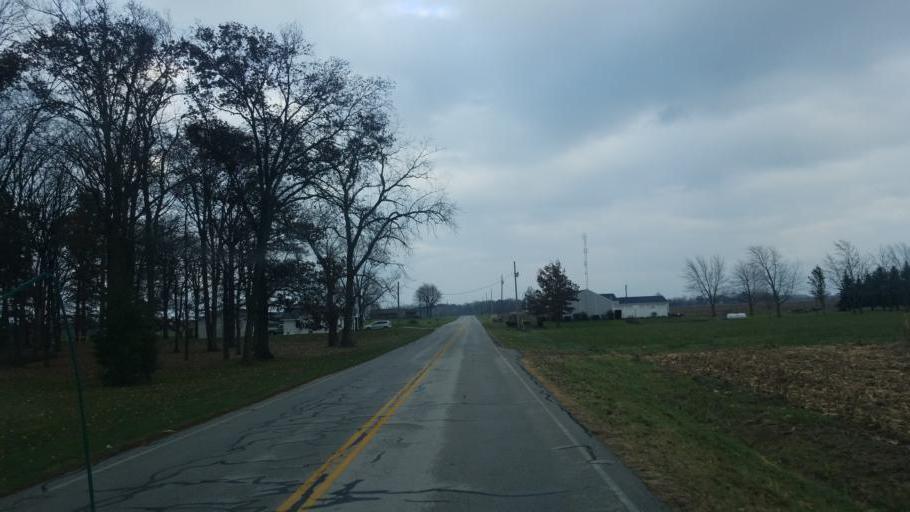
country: US
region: Ohio
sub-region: Mercer County
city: Coldwater
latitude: 40.5091
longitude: -84.6018
